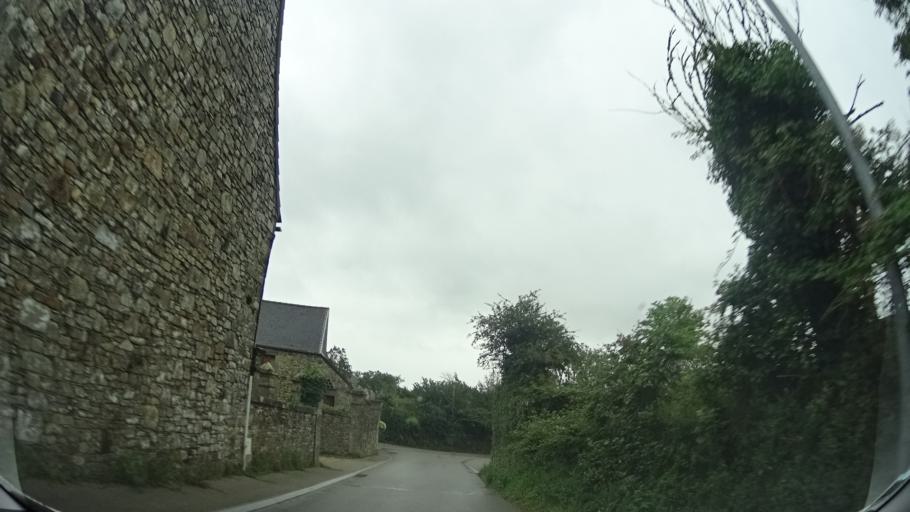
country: FR
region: Lower Normandy
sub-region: Departement de la Manche
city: Beaumont-Hague
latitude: 49.6115
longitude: -1.8228
